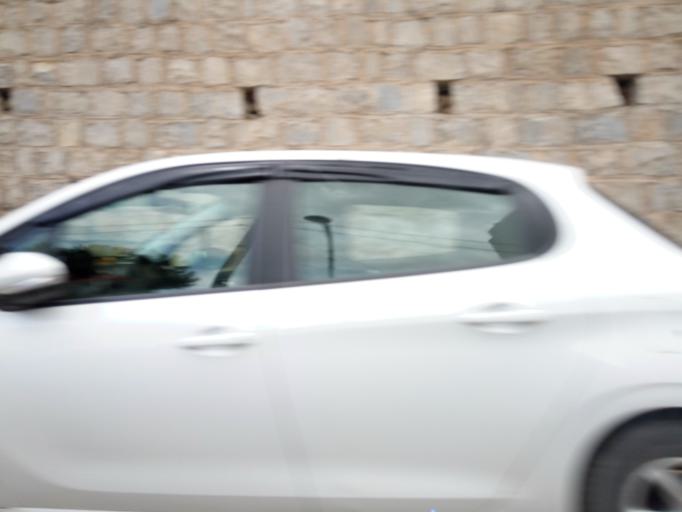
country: DZ
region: Constantine
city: Constantine
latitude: 36.3587
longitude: 6.6077
